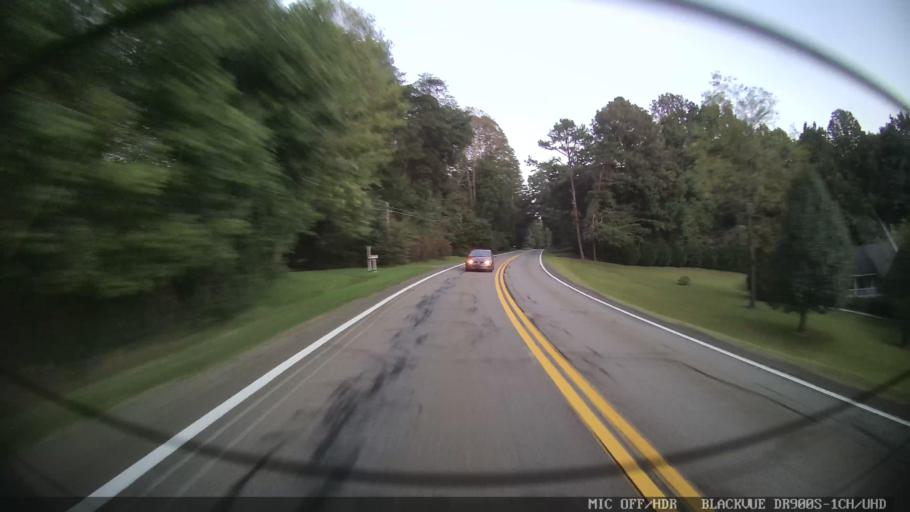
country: US
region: Georgia
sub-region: Gilmer County
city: Ellijay
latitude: 34.7347
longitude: -84.5144
